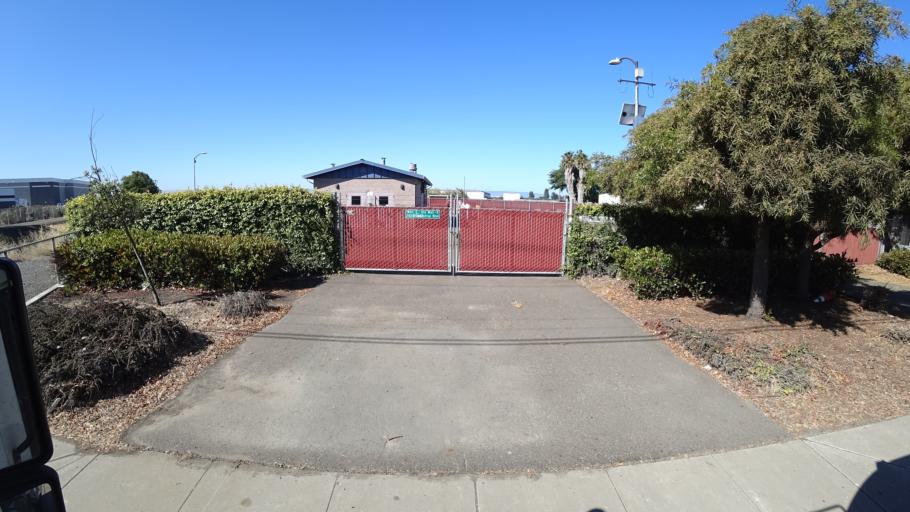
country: US
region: California
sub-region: Alameda County
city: Hayward
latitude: 37.6191
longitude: -122.0973
